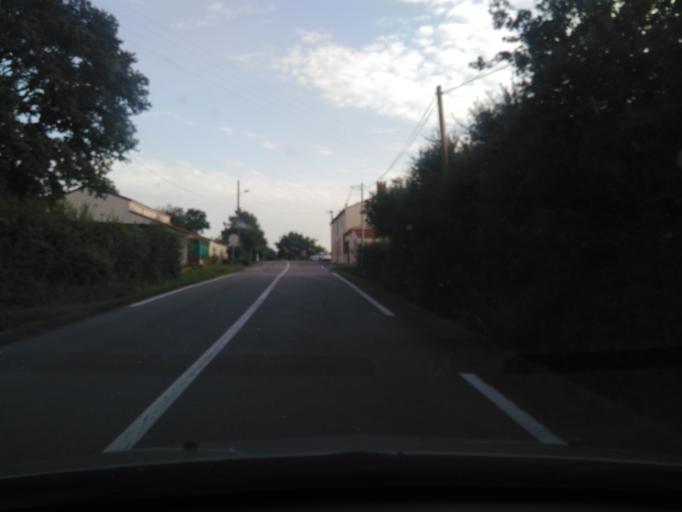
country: FR
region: Pays de la Loire
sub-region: Departement de la Vendee
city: Nesmy
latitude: 46.6250
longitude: -1.4076
